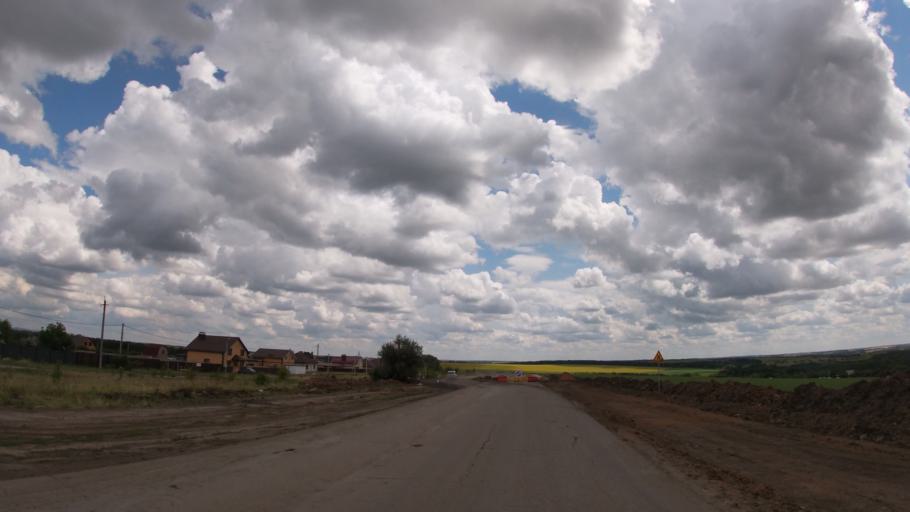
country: RU
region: Belgorod
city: Mayskiy
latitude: 50.5017
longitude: 36.4460
